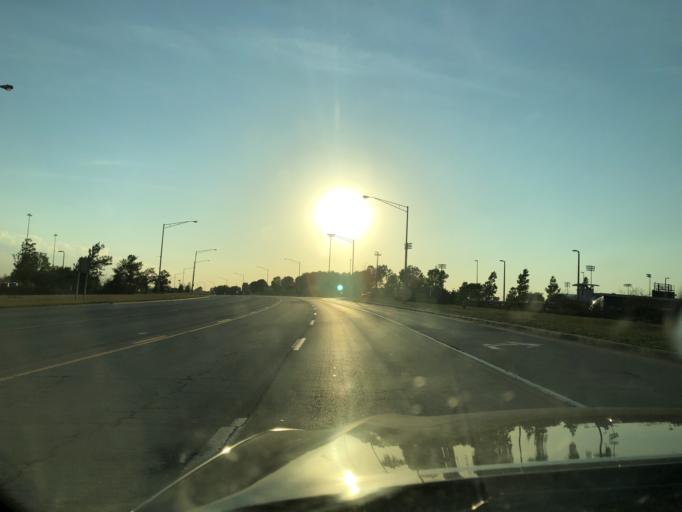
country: US
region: Kansas
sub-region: Wyandotte County
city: Edwardsville
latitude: 39.1230
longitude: -94.8277
